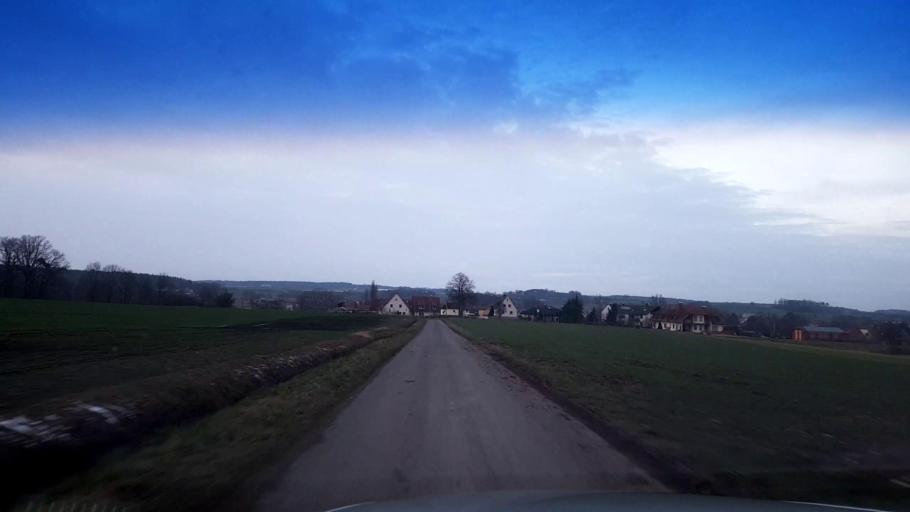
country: DE
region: Bavaria
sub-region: Upper Franconia
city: Frensdorf
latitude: 49.8168
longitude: 10.8347
